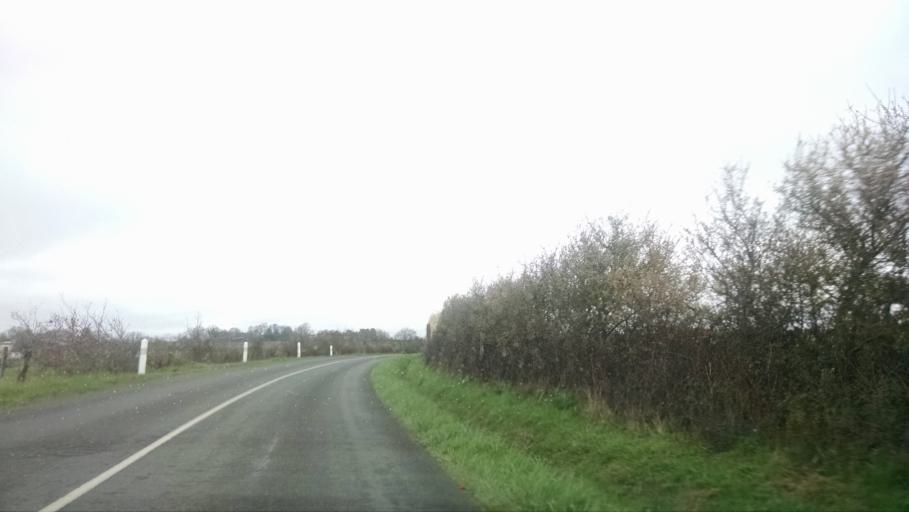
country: FR
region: Pays de la Loire
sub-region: Departement de la Loire-Atlantique
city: Aigrefeuille-sur-Maine
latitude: 47.0754
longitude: -1.3865
